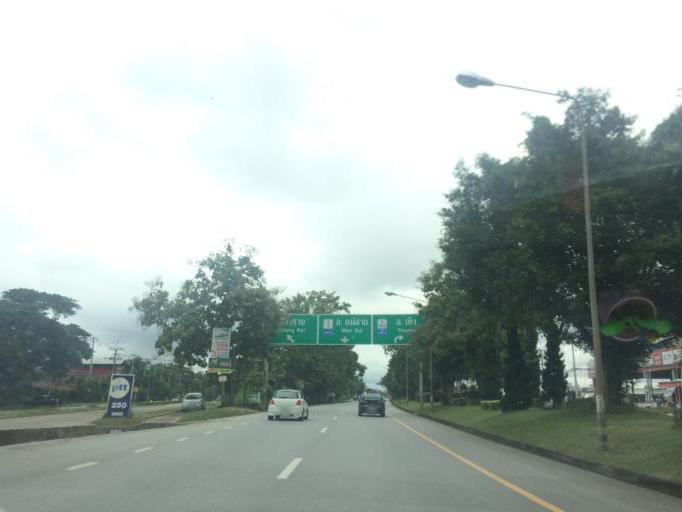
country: TH
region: Chiang Rai
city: Chiang Rai
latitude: 19.8728
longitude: 99.8273
